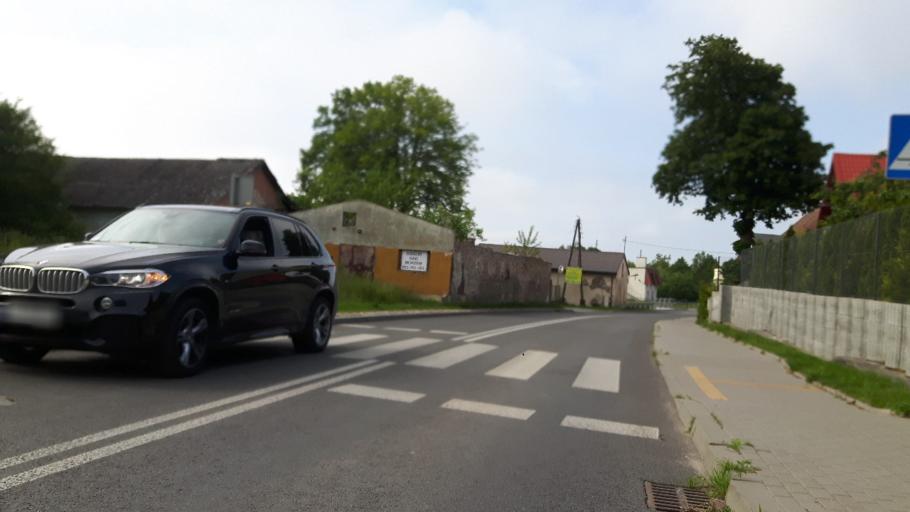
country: PL
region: West Pomeranian Voivodeship
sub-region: Powiat slawienski
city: Darlowo
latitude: 54.3548
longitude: 16.3347
